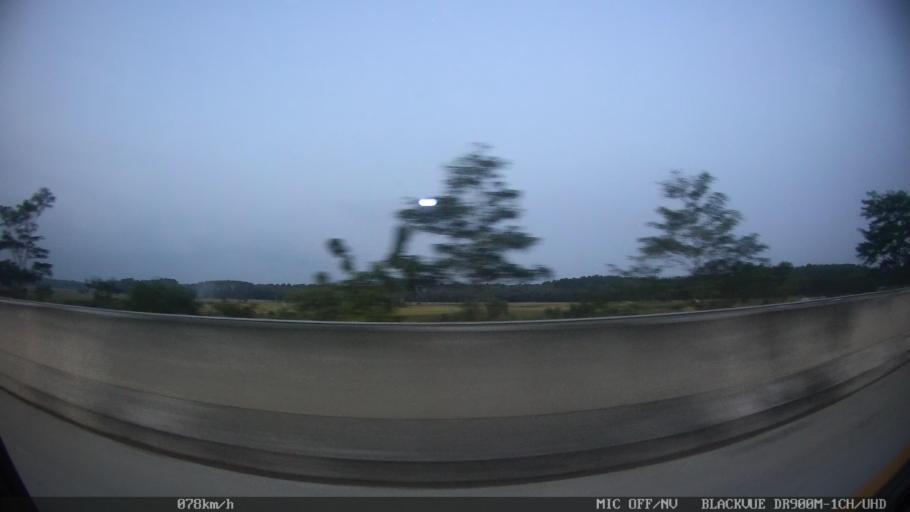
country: ID
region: Lampung
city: Sidorejo
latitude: -5.5916
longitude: 105.5478
